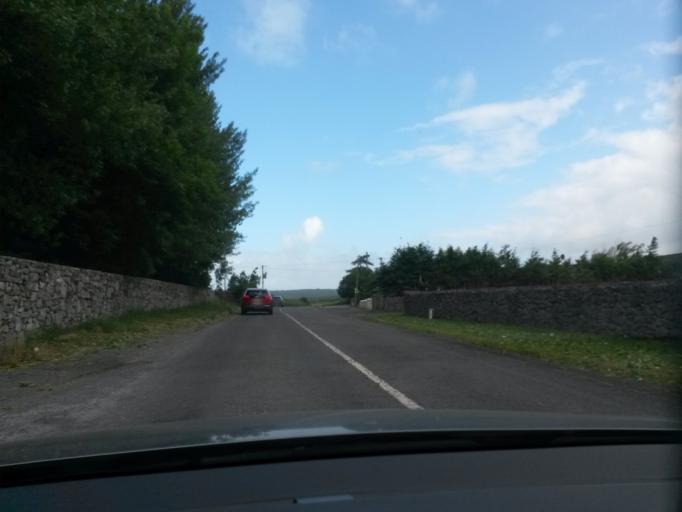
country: IE
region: Munster
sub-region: An Clar
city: Ennis
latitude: 52.9598
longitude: -9.0783
